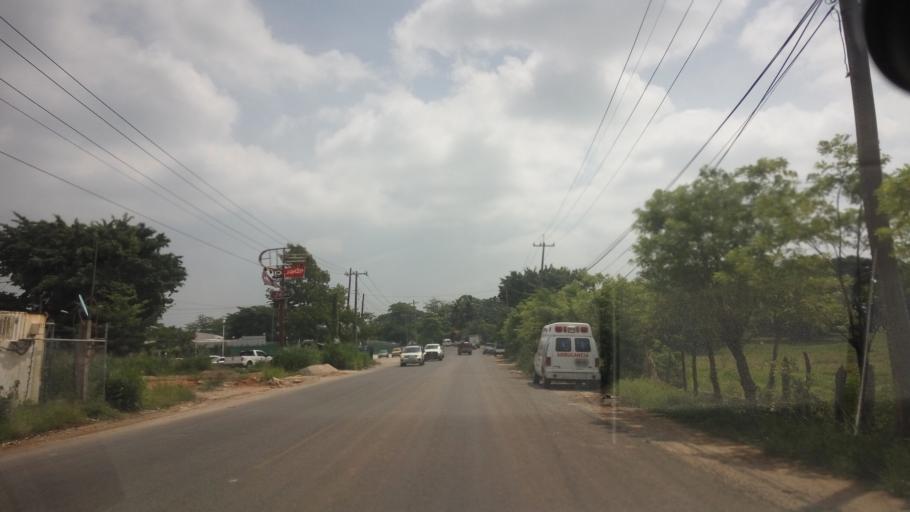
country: MX
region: Chiapas
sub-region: Reforma
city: El Carmen (El Limon)
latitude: 17.8846
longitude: -93.1455
